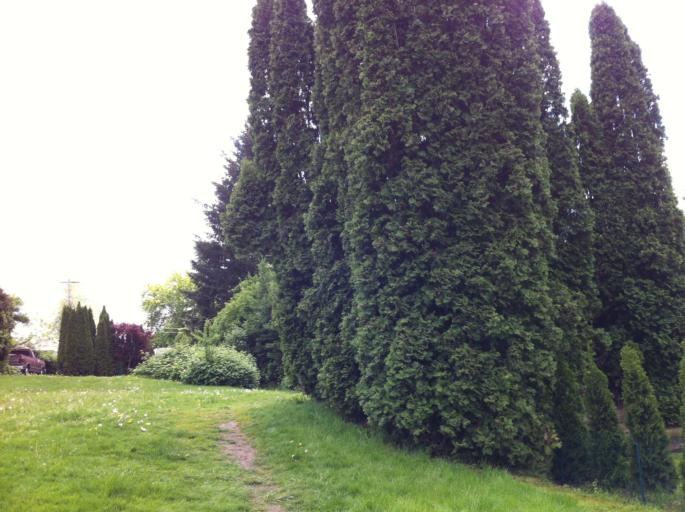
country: US
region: Oregon
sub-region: Washington County
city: Metzger
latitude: 45.4468
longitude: -122.7271
